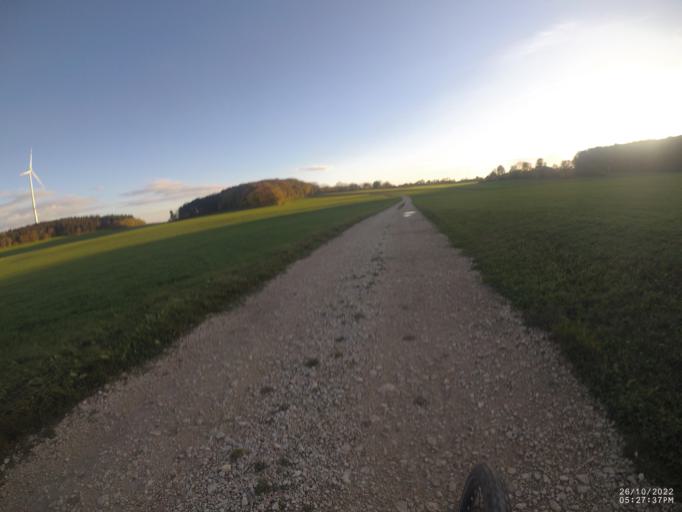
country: DE
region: Baden-Wuerttemberg
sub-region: Regierungsbezirk Stuttgart
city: Hohenstadt
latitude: 48.5462
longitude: 9.6897
